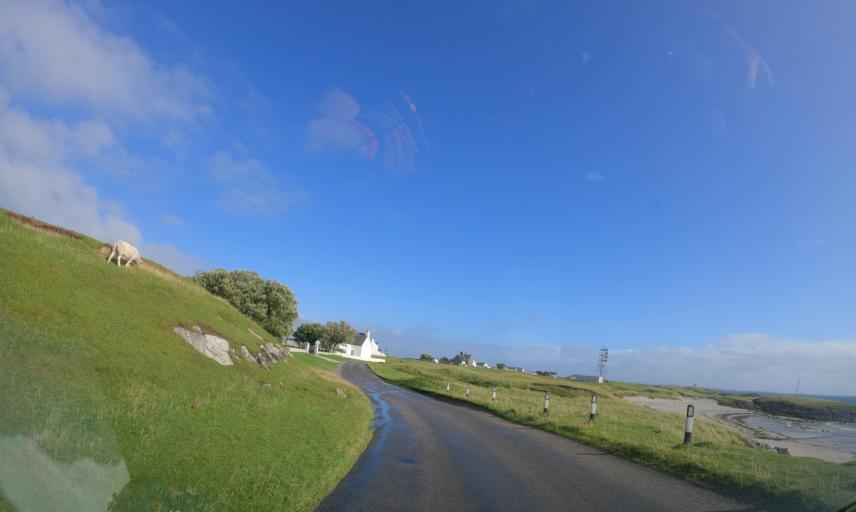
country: GB
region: Scotland
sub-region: Eilean Siar
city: Barra
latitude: 56.4977
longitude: -6.8103
